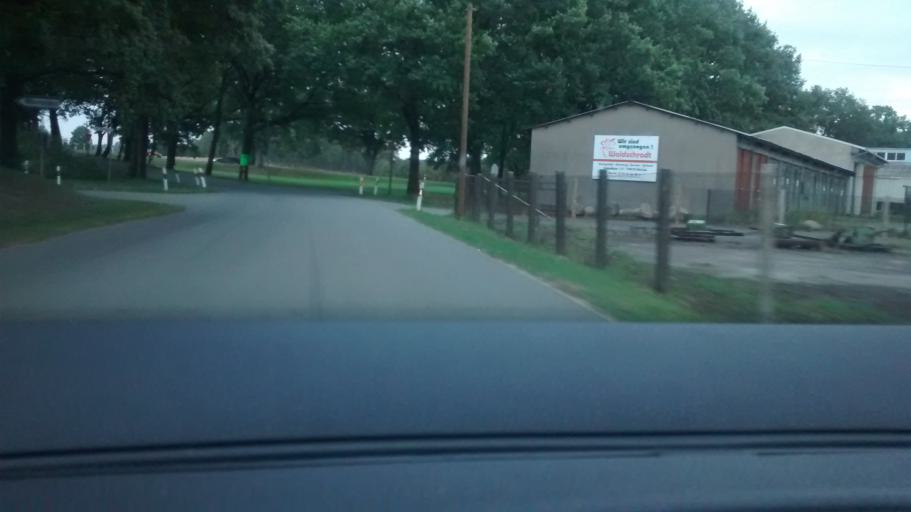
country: DE
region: Mecklenburg-Vorpommern
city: Lubtheen
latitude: 53.3978
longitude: 10.9802
